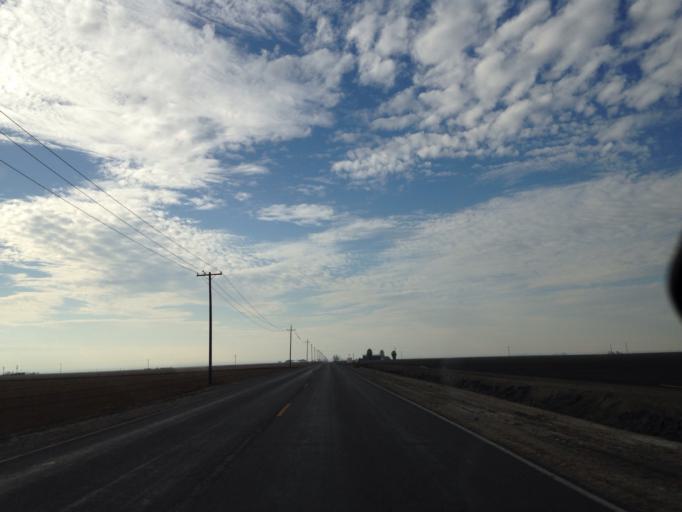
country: US
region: California
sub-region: Kern County
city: Buttonwillow
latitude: 35.4422
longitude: -119.5105
